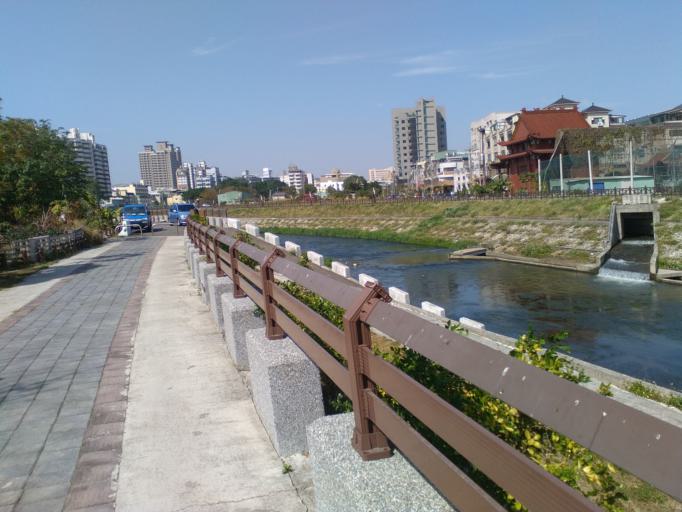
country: TW
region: Taiwan
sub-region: Taichung City
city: Taichung
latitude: 24.1118
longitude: 120.6721
